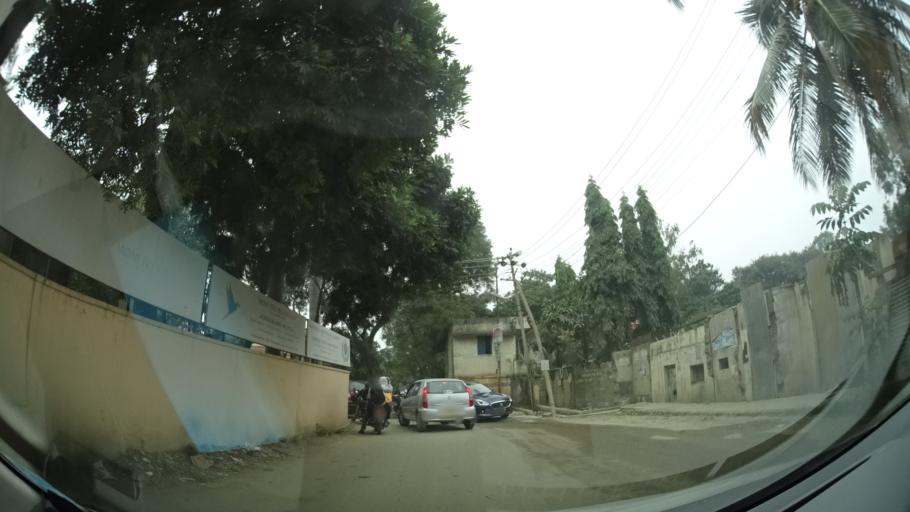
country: IN
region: Karnataka
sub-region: Bangalore Rural
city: Hoskote
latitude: 12.9767
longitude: 77.7397
